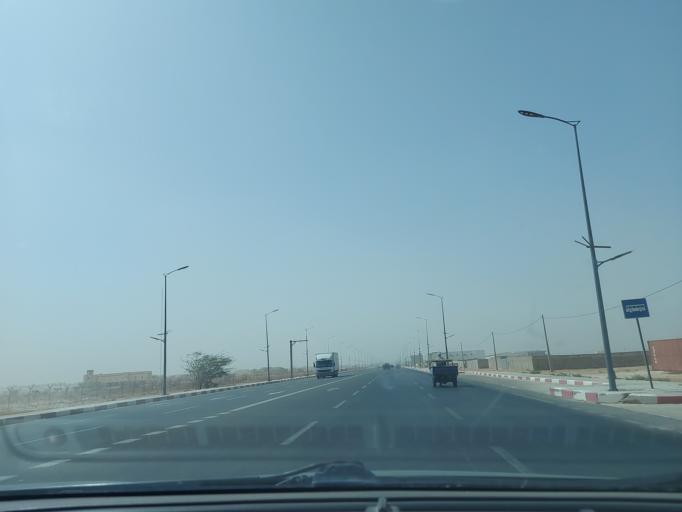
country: MR
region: Nouakchott
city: Nouakchott
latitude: 18.1402
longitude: -16.0062
